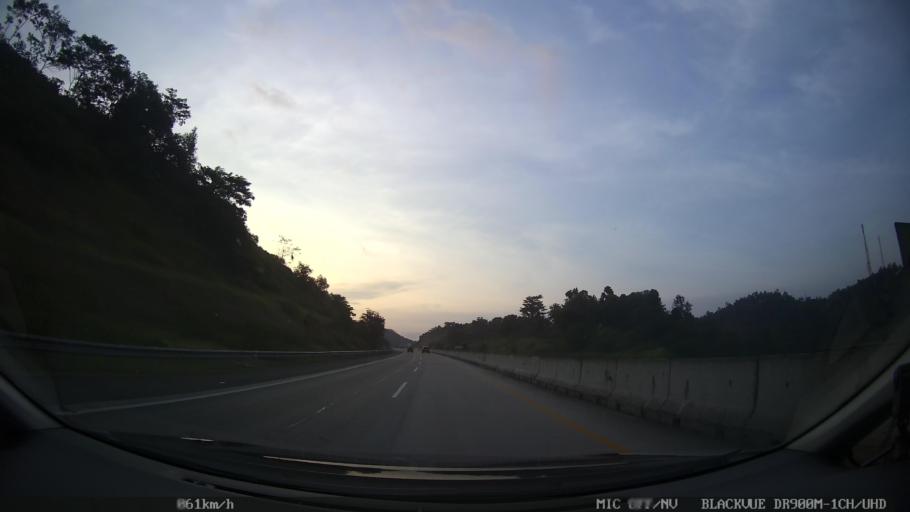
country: ID
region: Lampung
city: Penengahan
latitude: -5.8641
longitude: 105.7432
